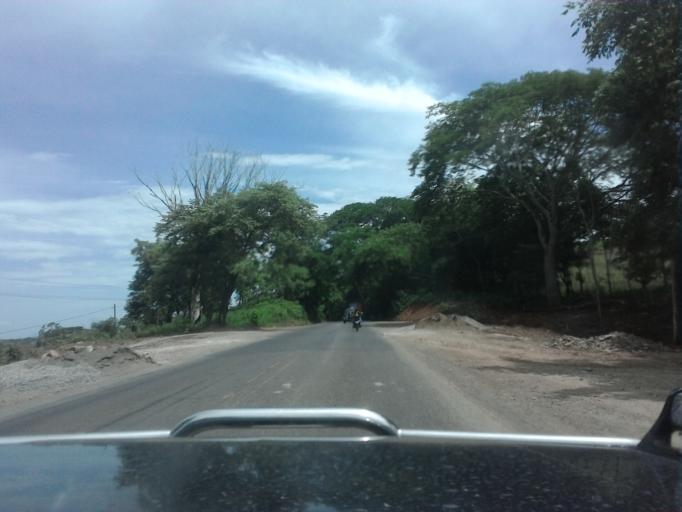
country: CR
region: Puntarenas
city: Miramar
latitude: 10.0667
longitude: -84.7653
